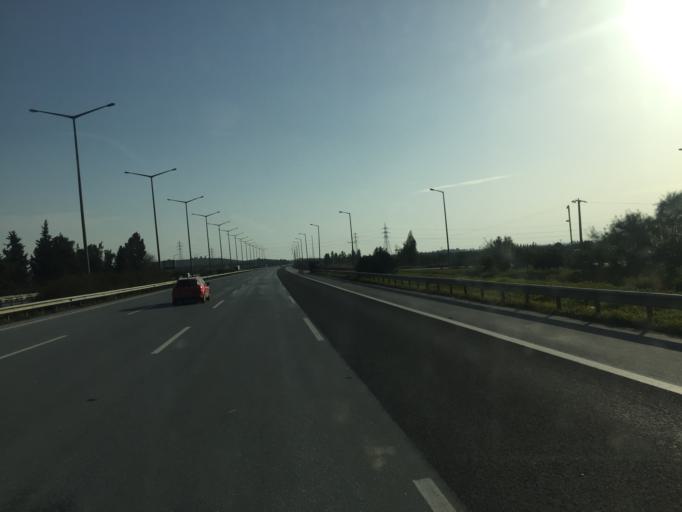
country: TR
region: Mersin
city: Yenice
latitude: 37.0236
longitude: 35.0633
